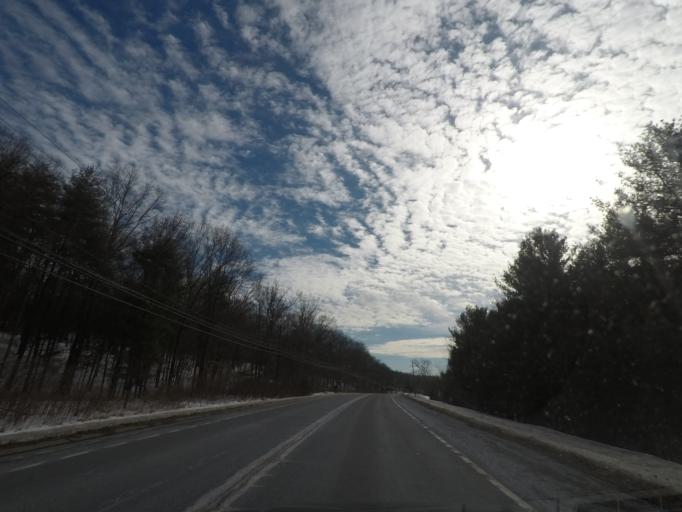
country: US
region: New York
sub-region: Albany County
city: Voorheesville
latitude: 42.6684
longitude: -73.9128
